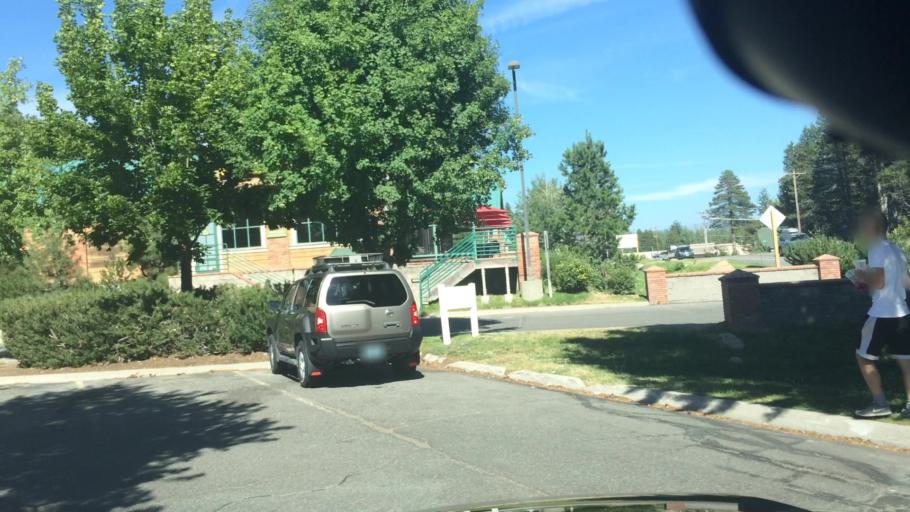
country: US
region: California
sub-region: Nevada County
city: Truckee
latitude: 39.3263
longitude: -120.2064
